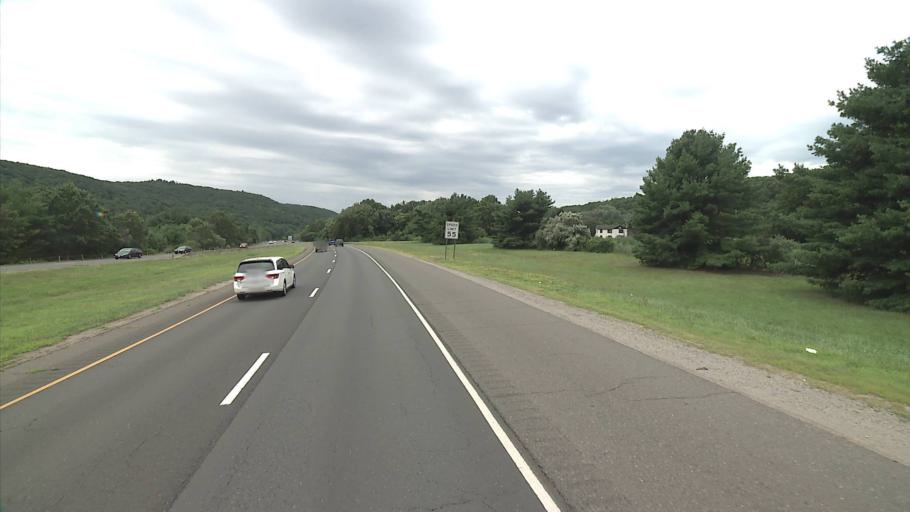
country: US
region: Connecticut
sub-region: New Haven County
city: Seymour
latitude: 41.4374
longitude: -73.0677
